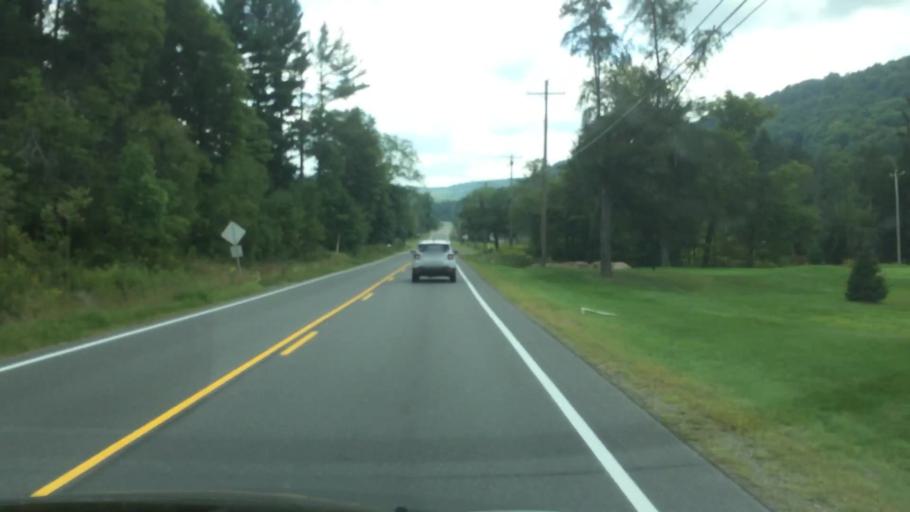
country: US
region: Pennsylvania
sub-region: McKean County
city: Bradford
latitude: 41.9022
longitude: -78.6116
